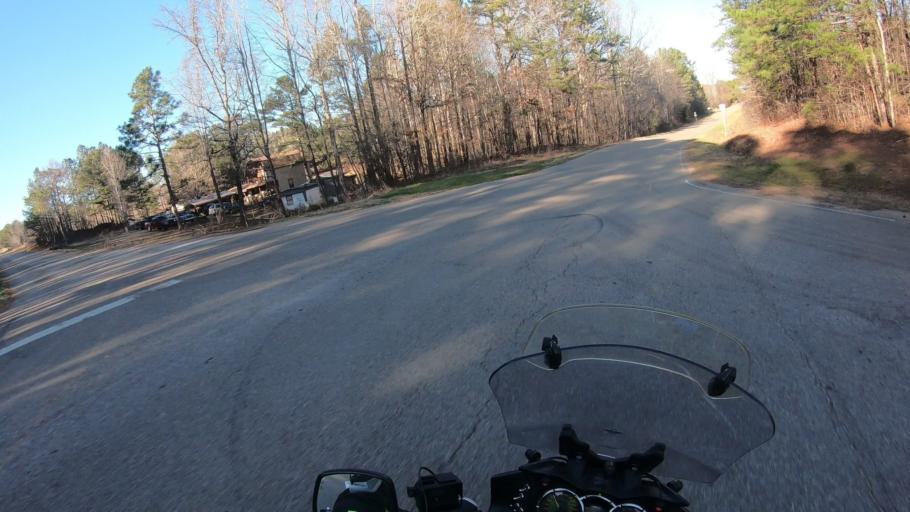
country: US
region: Georgia
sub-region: Haralson County
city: Tallapoosa
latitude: 33.8269
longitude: -85.4316
